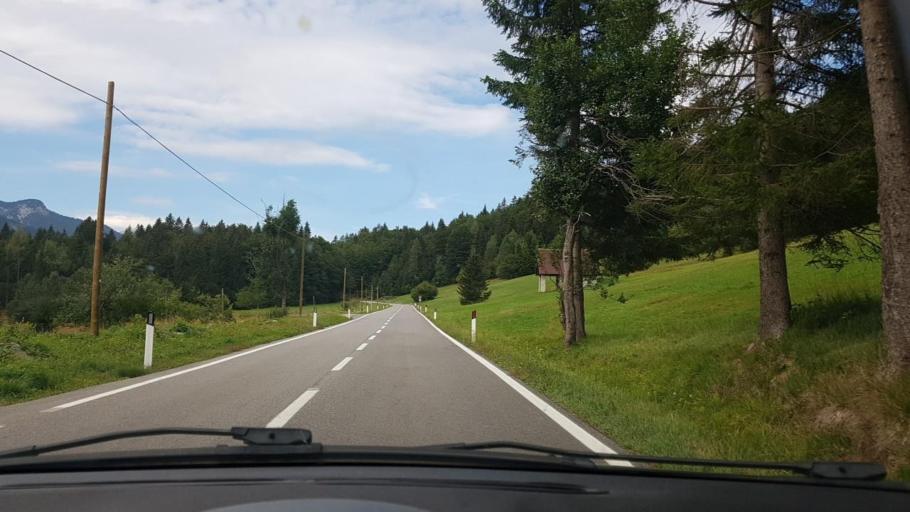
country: AT
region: Carinthia
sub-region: Politischer Bezirk Villach Land
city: Arnoldstein
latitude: 46.4993
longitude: 13.6809
